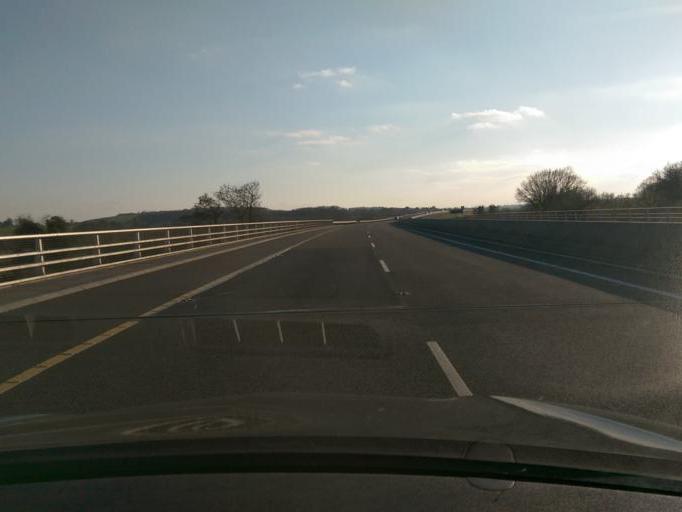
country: IE
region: Leinster
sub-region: Laois
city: Mountrath
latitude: 52.9458
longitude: -7.4469
